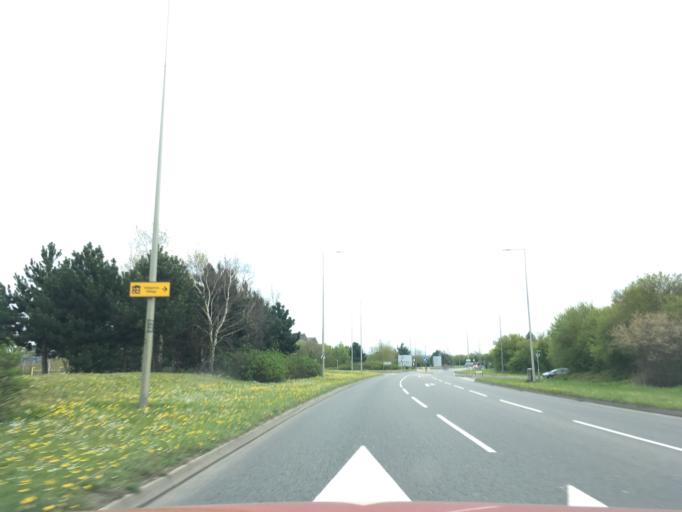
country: GB
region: England
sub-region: Milton Keynes
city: Broughton
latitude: 52.0404
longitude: -0.7120
